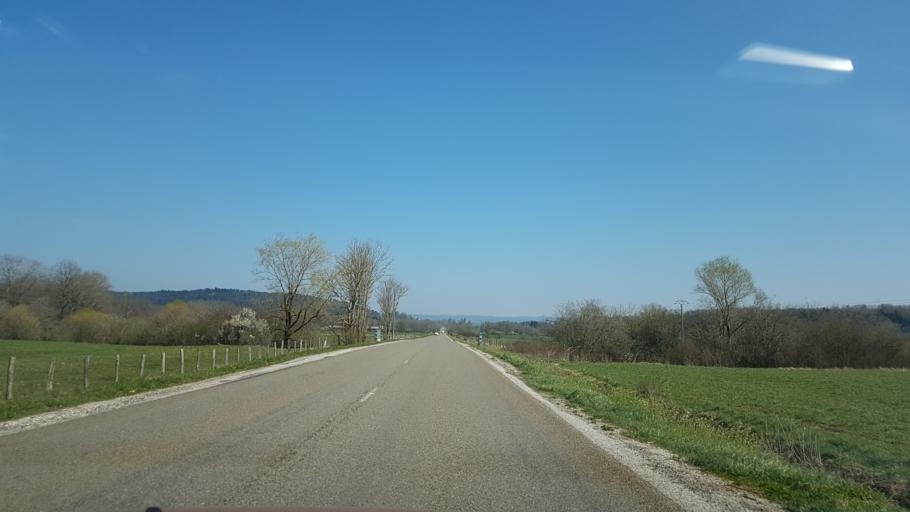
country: FR
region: Franche-Comte
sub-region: Departement du Jura
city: Orgelet
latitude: 46.5251
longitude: 5.5742
